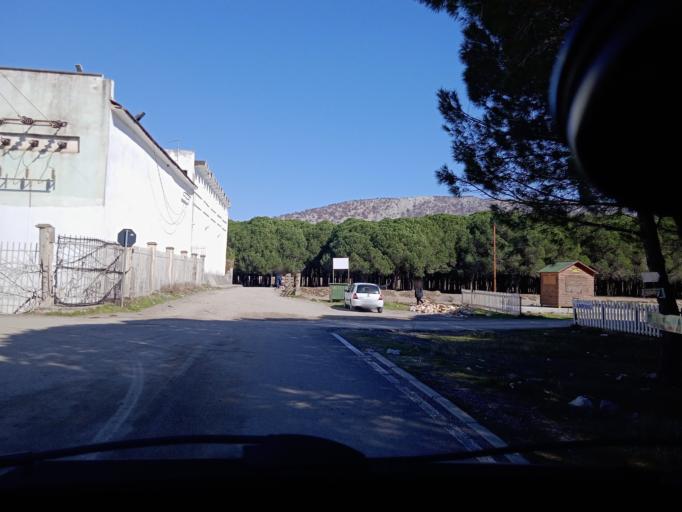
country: AL
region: Shkoder
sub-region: Rrethi i Shkodres
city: Velipoje
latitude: 41.8635
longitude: 19.4416
